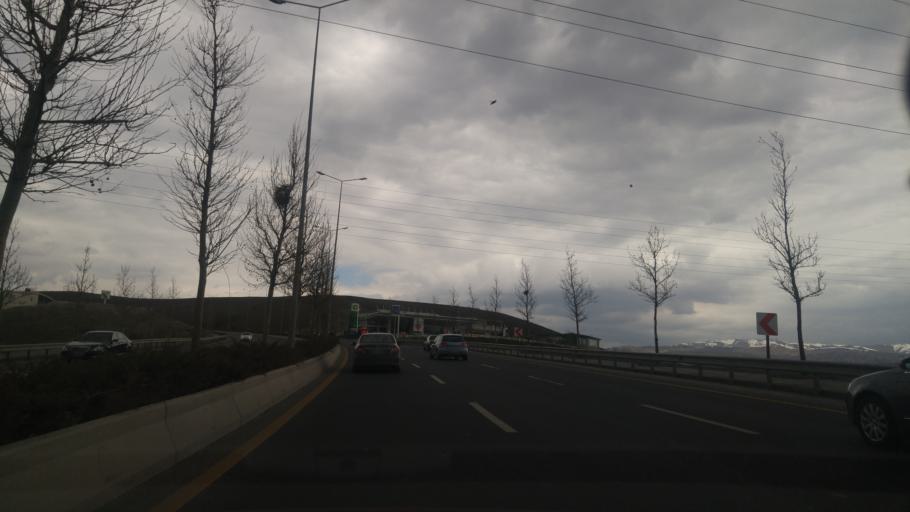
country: TR
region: Ankara
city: Mamak
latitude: 39.8852
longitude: 32.9167
